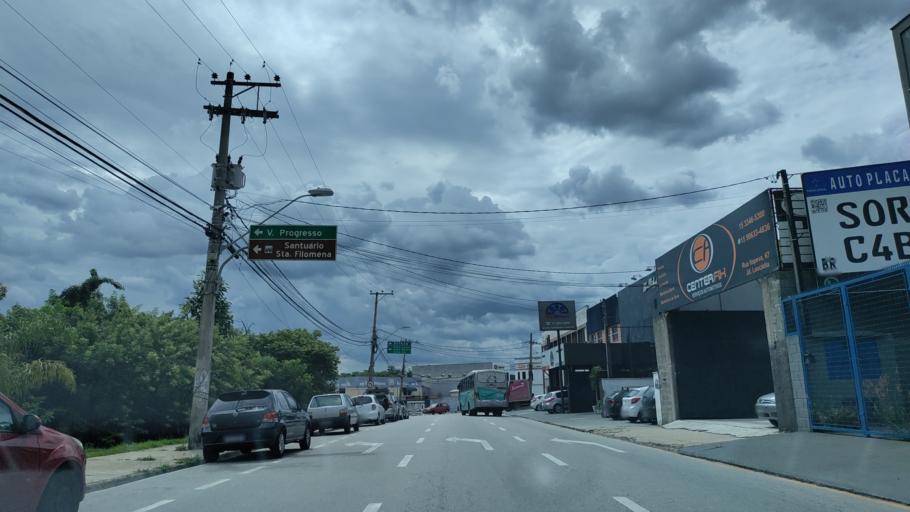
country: BR
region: Sao Paulo
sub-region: Sorocaba
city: Sorocaba
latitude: -23.4763
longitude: -47.4405
